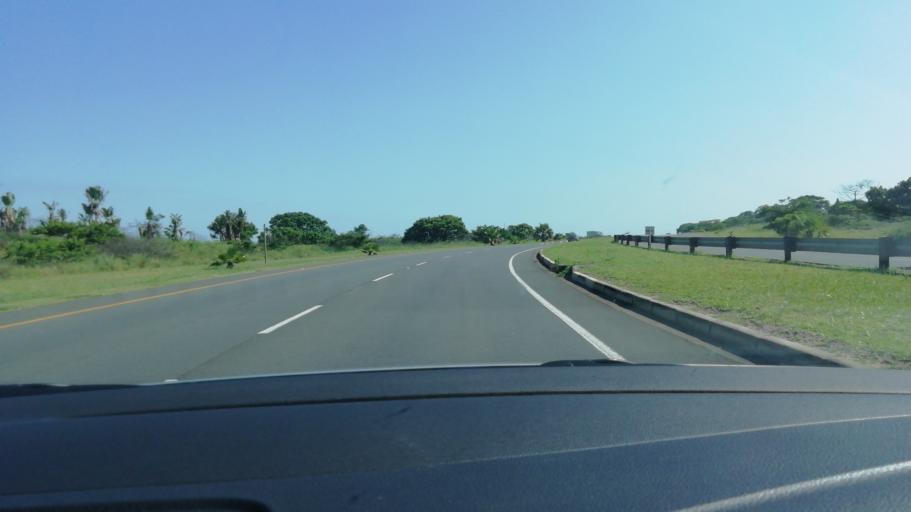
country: ZA
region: KwaZulu-Natal
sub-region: uThungulu District Municipality
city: Richards Bay
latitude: -28.7660
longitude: 32.0483
